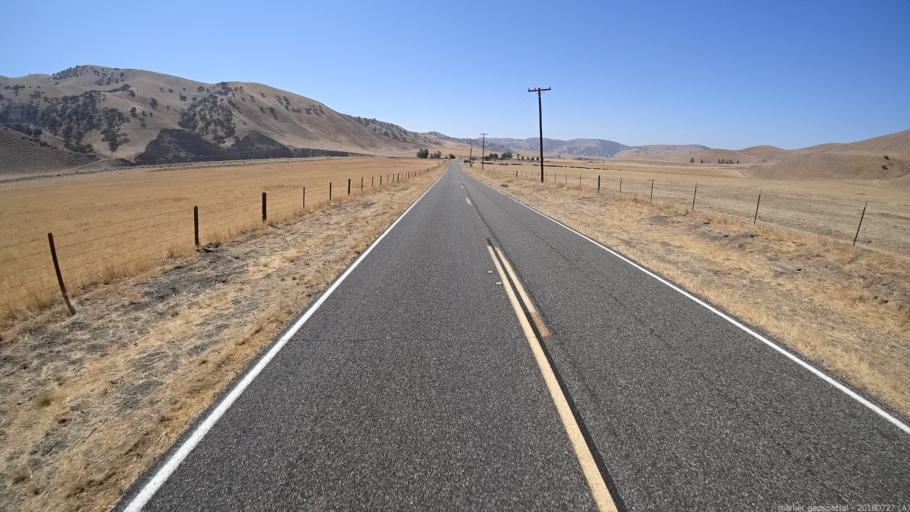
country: US
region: California
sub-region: Monterey County
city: King City
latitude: 36.3056
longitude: -120.9288
